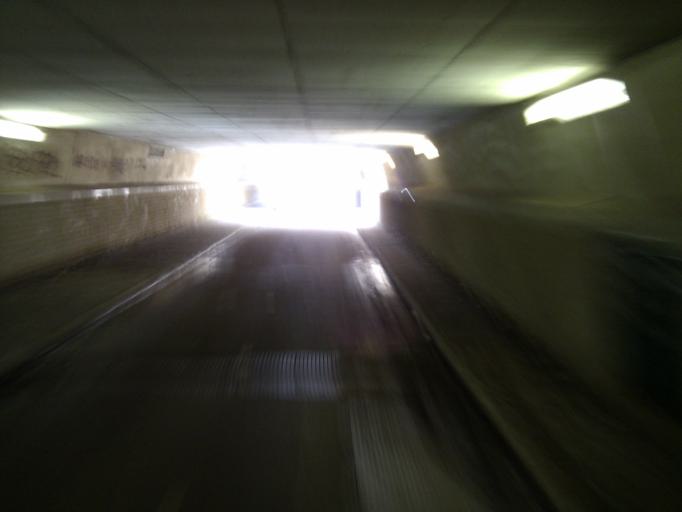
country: NL
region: Utrecht
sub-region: Gemeente De Bilt
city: De Bilt
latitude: 52.0924
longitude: 5.1763
